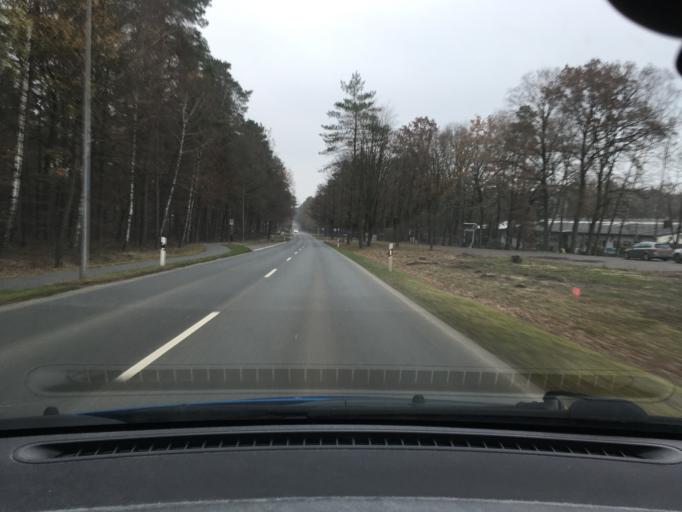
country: DE
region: Lower Saxony
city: Soltau
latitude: 52.9962
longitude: 9.8532
